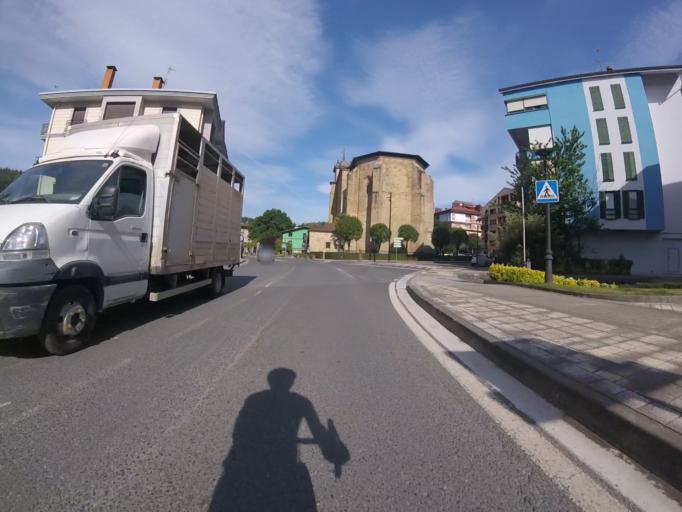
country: ES
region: Basque Country
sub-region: Provincia de Guipuzcoa
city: Ormaiztegui
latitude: 43.0429
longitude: -2.2533
